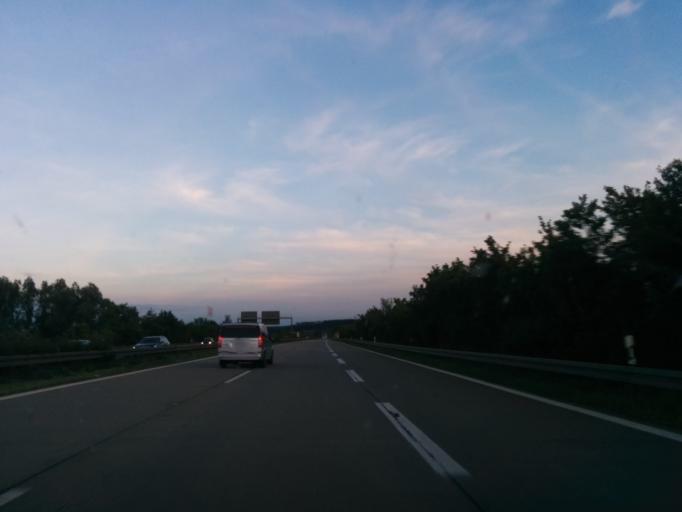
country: DE
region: Bavaria
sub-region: Regierungsbezirk Mittelfranken
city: Schnelldorf
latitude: 49.1949
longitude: 10.2362
